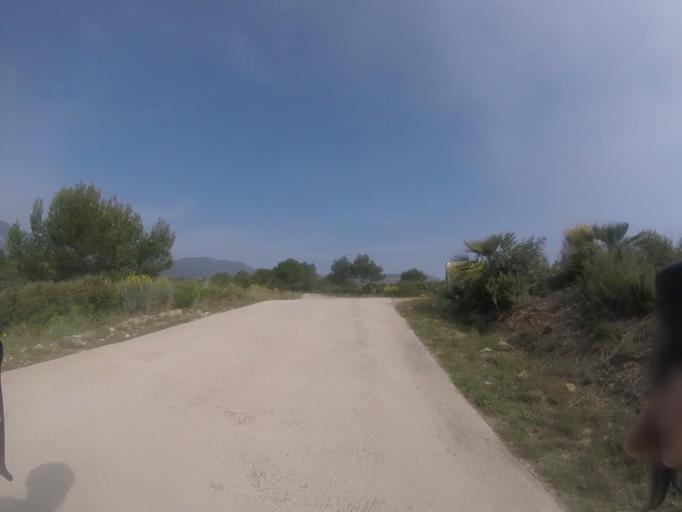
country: ES
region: Valencia
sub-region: Provincia de Castello
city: Alcoceber
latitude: 40.2795
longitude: 0.3274
